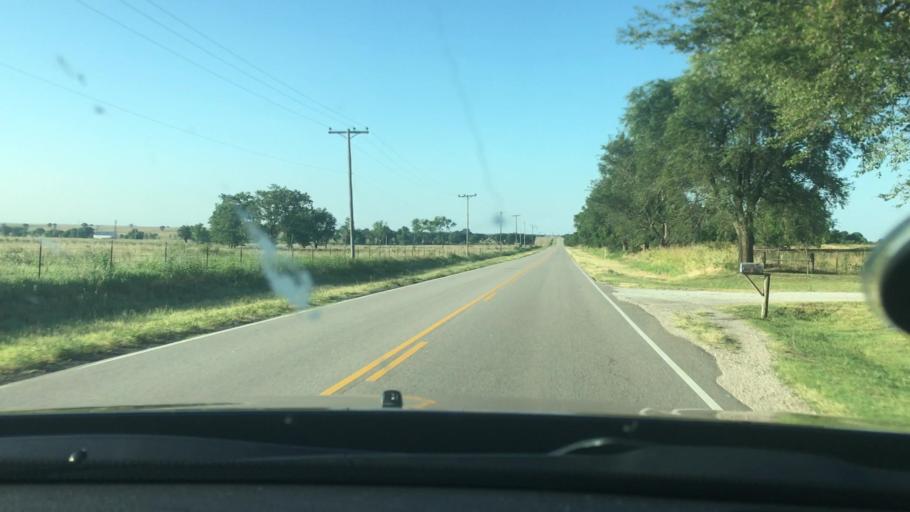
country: US
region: Oklahoma
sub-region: Murray County
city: Sulphur
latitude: 34.6075
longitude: -96.8449
